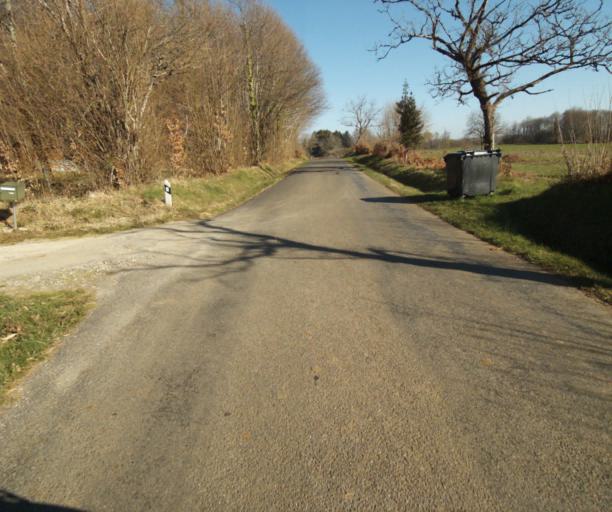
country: FR
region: Limousin
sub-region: Departement de la Correze
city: Saint-Clement
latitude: 45.3723
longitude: 1.6463
